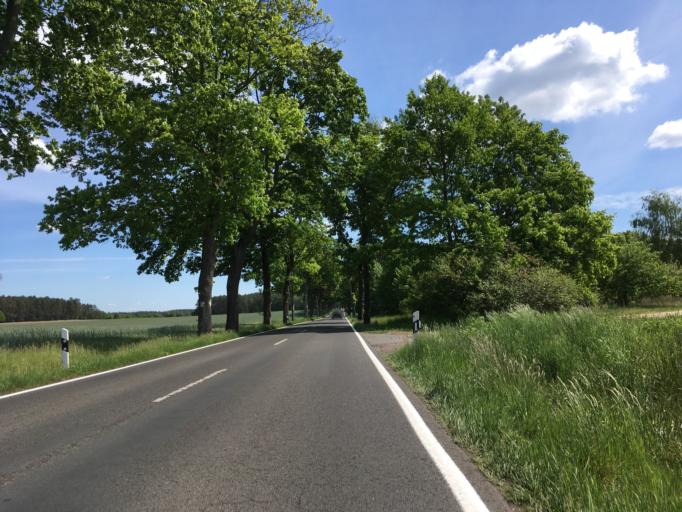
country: DE
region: Brandenburg
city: Biesenthal
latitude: 52.7691
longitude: 13.6529
